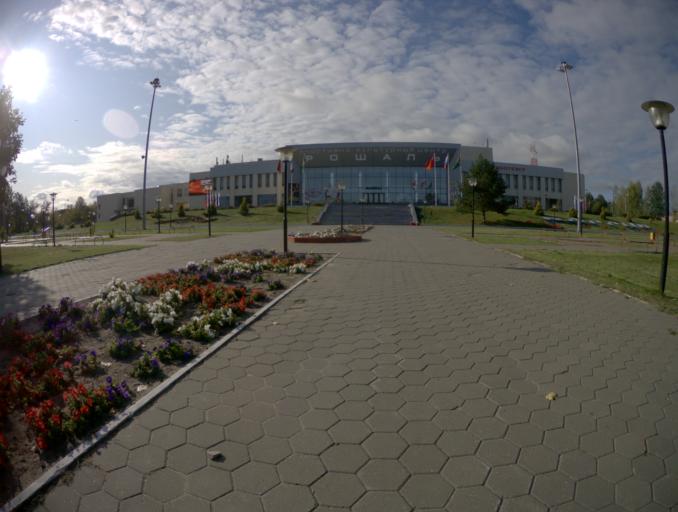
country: RU
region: Moskovskaya
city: Roshal'
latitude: 55.6635
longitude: 39.8626
